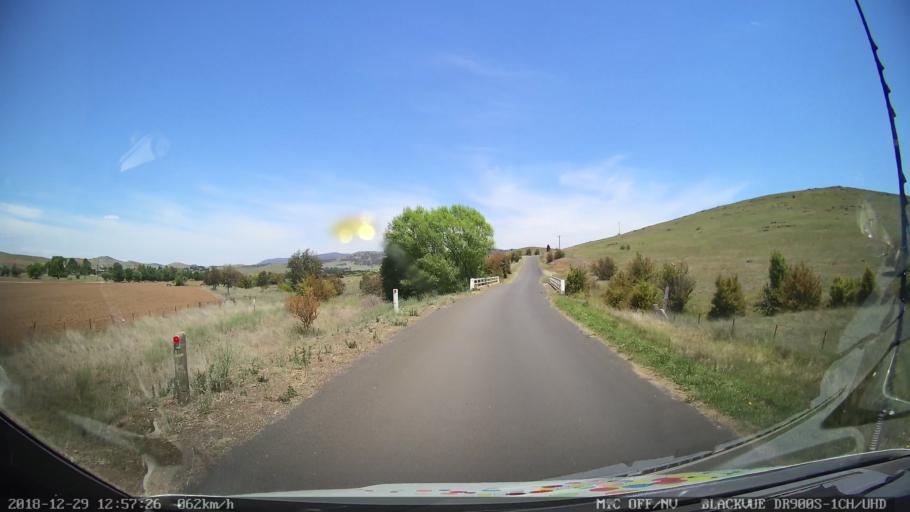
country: AU
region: Australian Capital Territory
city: Macarthur
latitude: -35.7082
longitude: 149.1774
